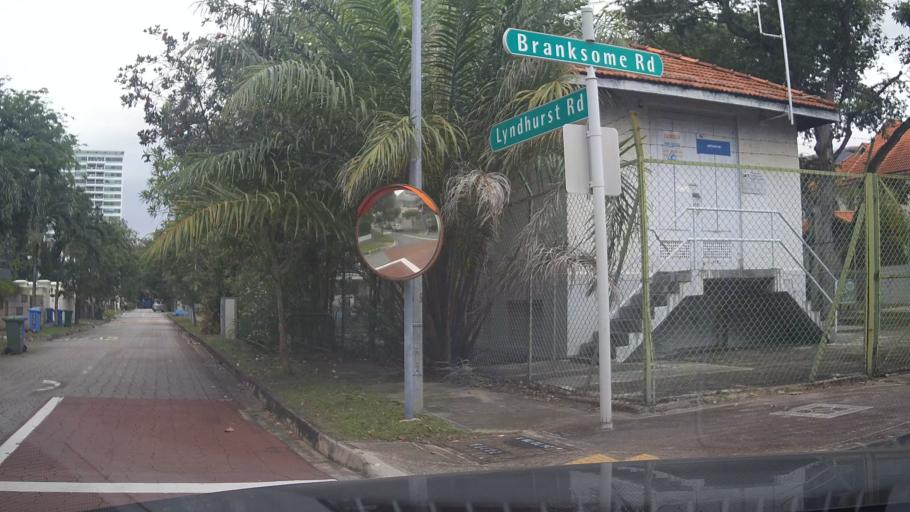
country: SG
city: Singapore
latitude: 1.3033
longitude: 103.8881
